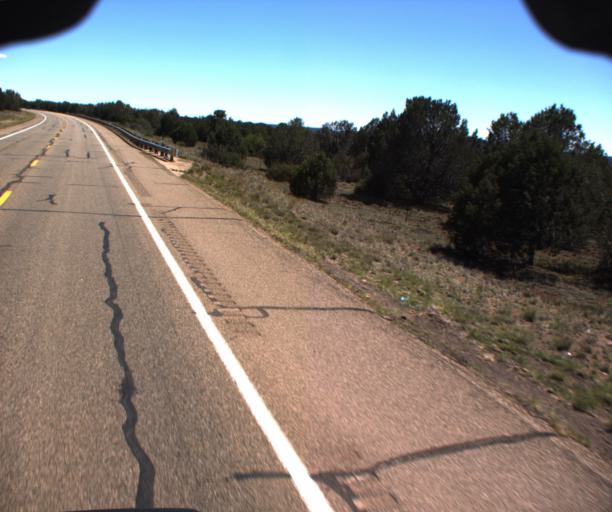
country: US
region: Arizona
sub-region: Yavapai County
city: Paulden
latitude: 35.1099
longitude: -112.4304
